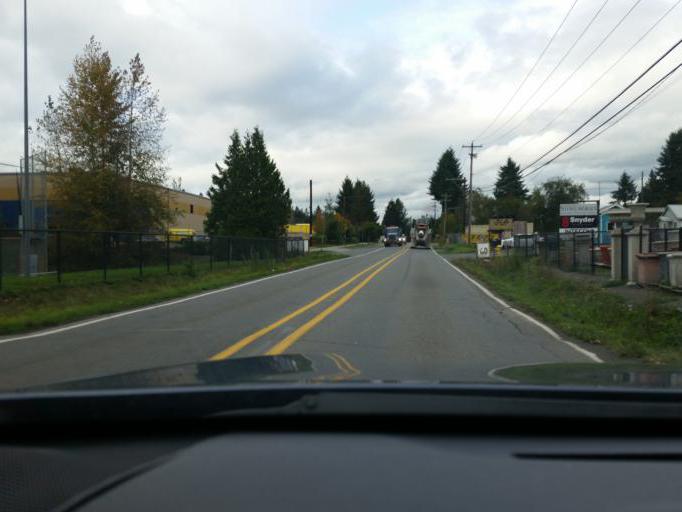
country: US
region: Washington
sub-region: Snohomish County
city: Maltby
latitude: 47.8134
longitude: -122.1100
